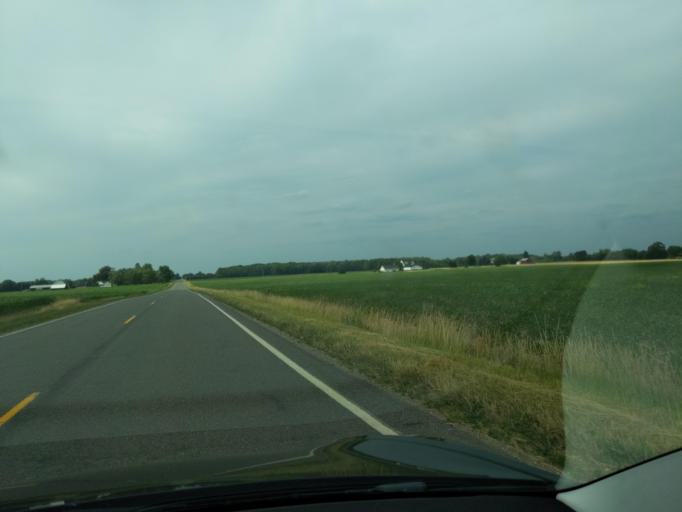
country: US
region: Michigan
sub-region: Clinton County
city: DeWitt
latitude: 42.9091
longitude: -84.6021
